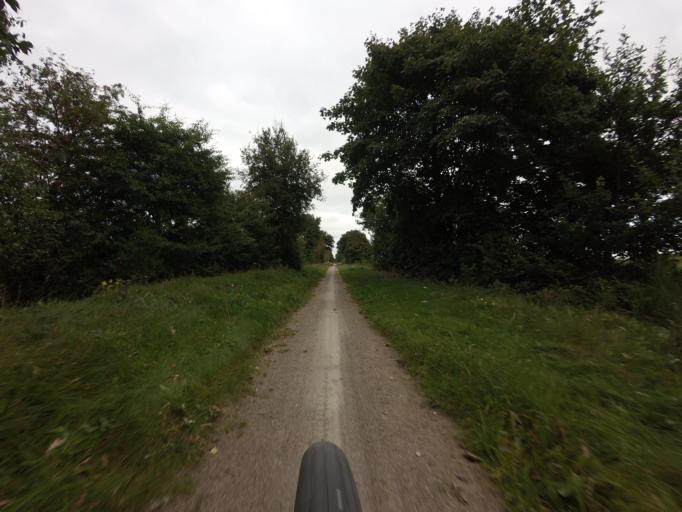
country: DK
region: South Denmark
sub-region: Billund Kommune
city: Grindsted
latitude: 55.7978
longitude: 8.9947
